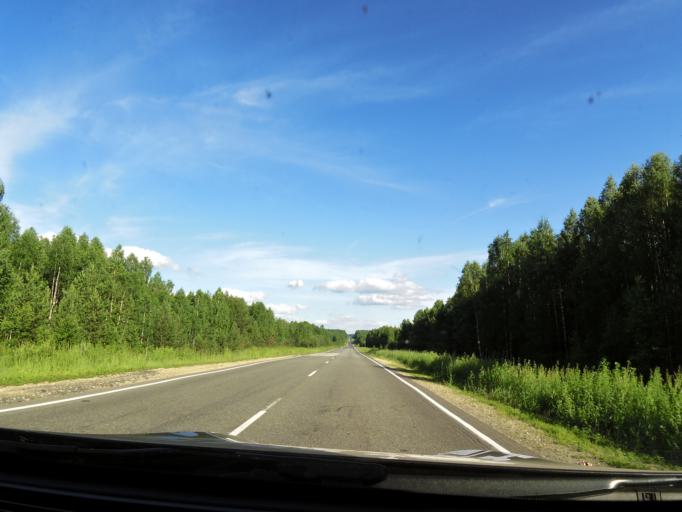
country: RU
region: Kirov
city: Chernaya Kholunitsa
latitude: 58.8094
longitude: 51.8390
